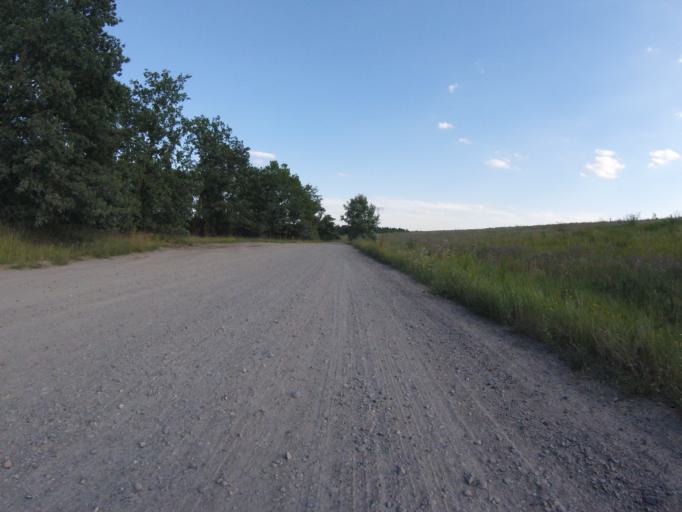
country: DE
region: Brandenburg
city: Zossen
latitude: 52.2132
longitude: 13.4795
